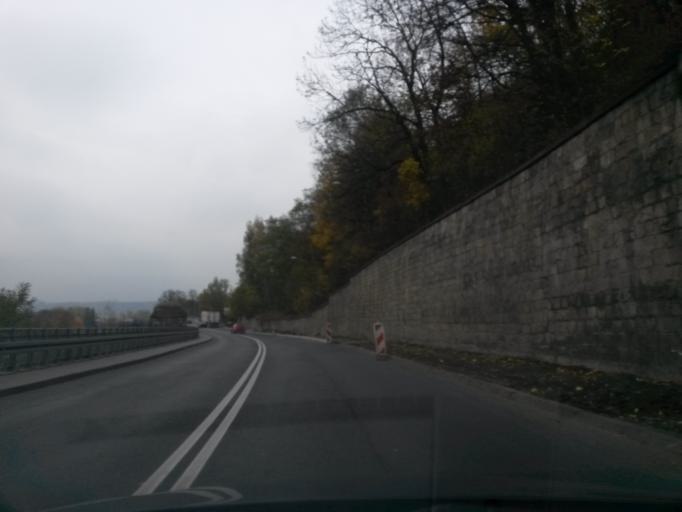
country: PL
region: Lower Silesian Voivodeship
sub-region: Powiat klodzki
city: Klodzko
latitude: 50.4431
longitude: 16.6602
